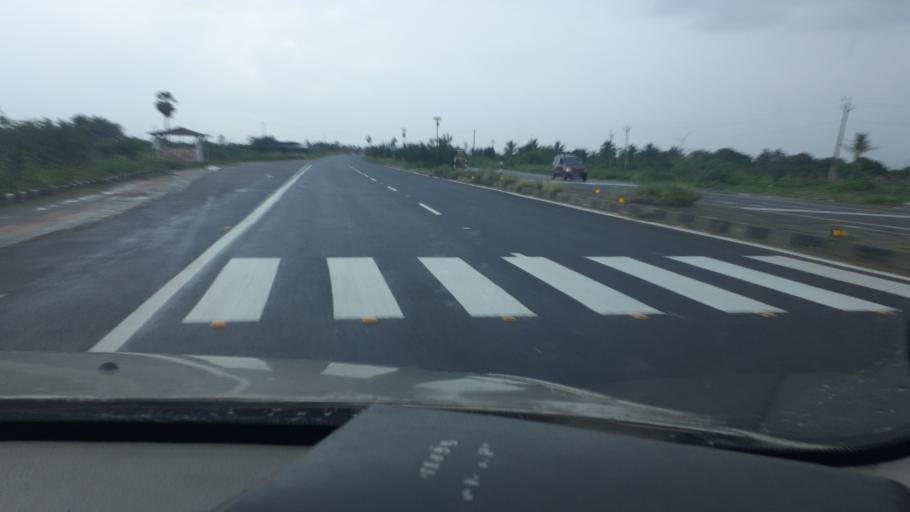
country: IN
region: Tamil Nadu
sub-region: Thoothukkudi
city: Kadambur
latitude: 9.0477
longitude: 77.7947
